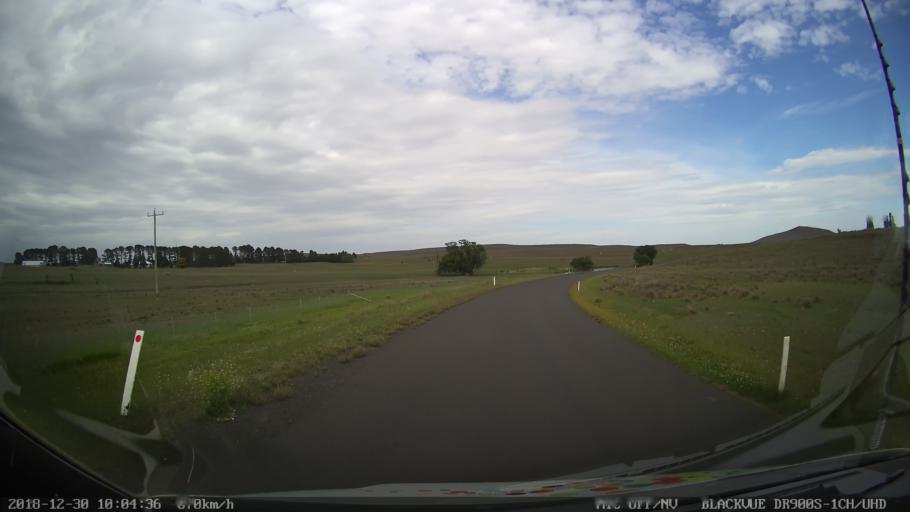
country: AU
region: New South Wales
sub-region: Cooma-Monaro
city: Cooma
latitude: -36.5229
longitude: 149.1448
